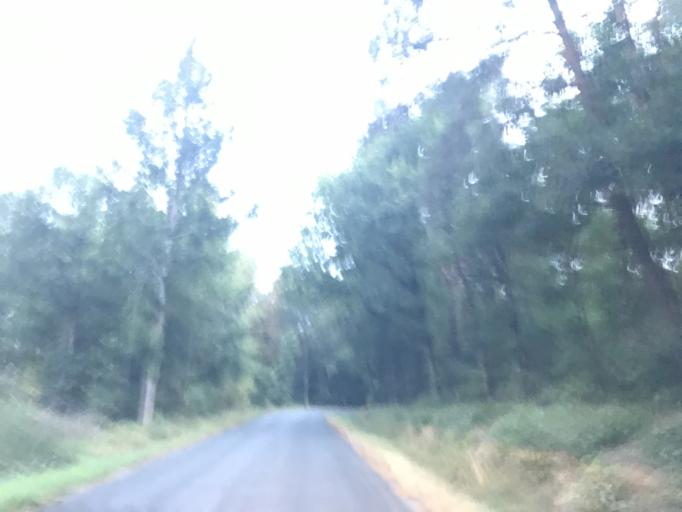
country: FR
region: Auvergne
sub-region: Departement du Puy-de-Dome
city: Escoutoux
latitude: 45.7955
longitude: 3.5658
